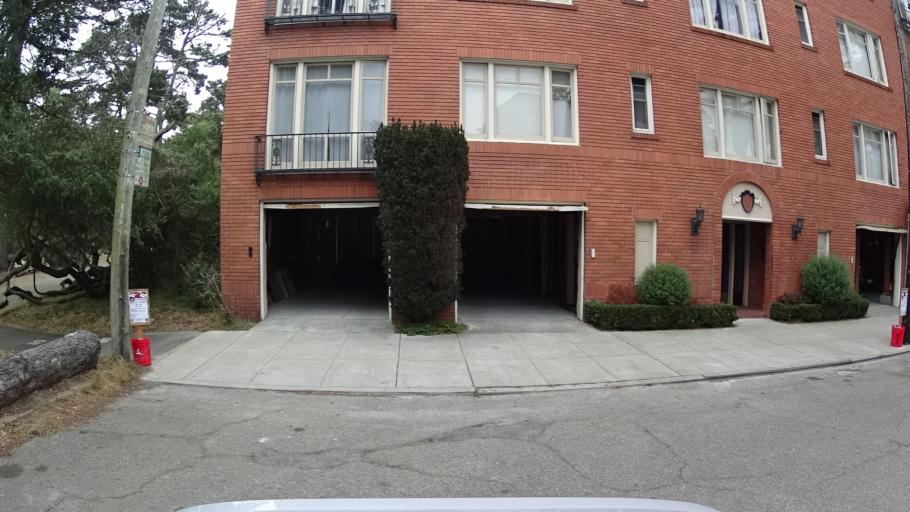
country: US
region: California
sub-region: San Francisco County
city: San Francisco
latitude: 37.7868
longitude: -122.4690
